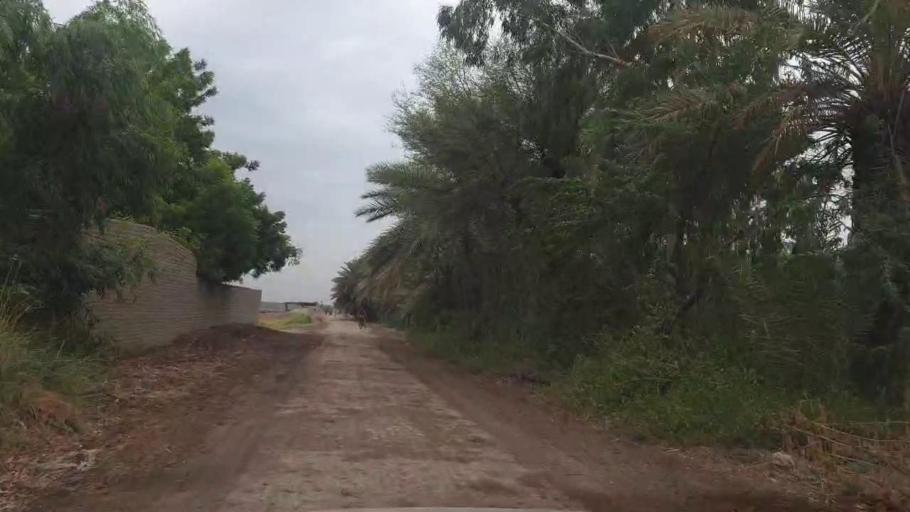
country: PK
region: Sindh
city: Khairpur
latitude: 27.5922
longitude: 68.8135
